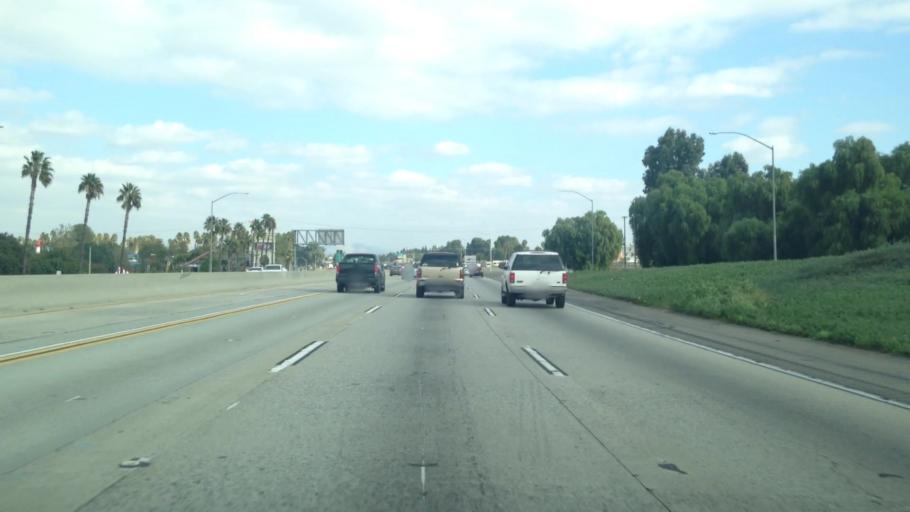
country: US
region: California
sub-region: Riverside County
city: Home Gardens
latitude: 33.9023
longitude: -117.4778
